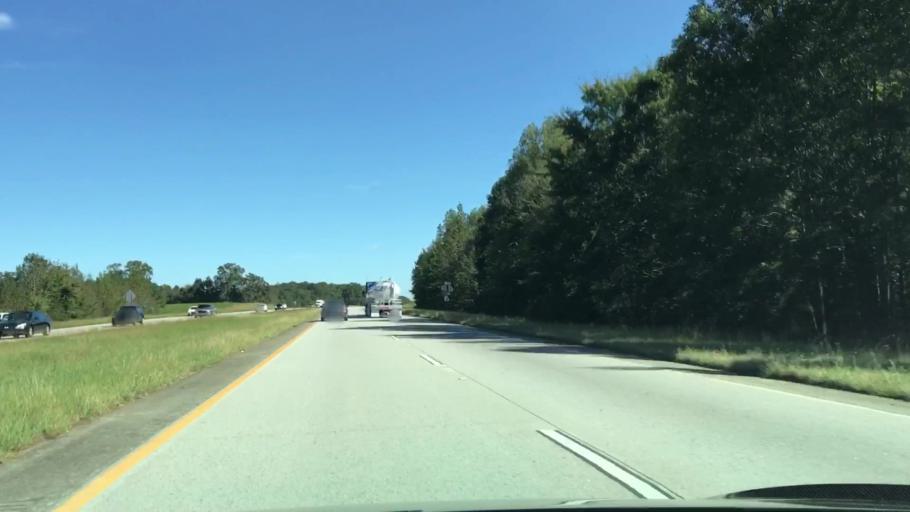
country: US
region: Georgia
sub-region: Oconee County
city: Bogart
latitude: 33.9422
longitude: -83.5616
